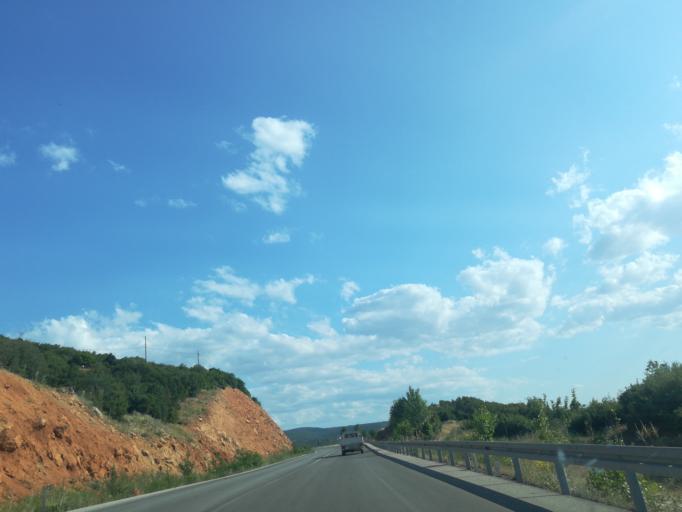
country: TR
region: Denizli
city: Ishakli
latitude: 38.1587
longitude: 30.0837
